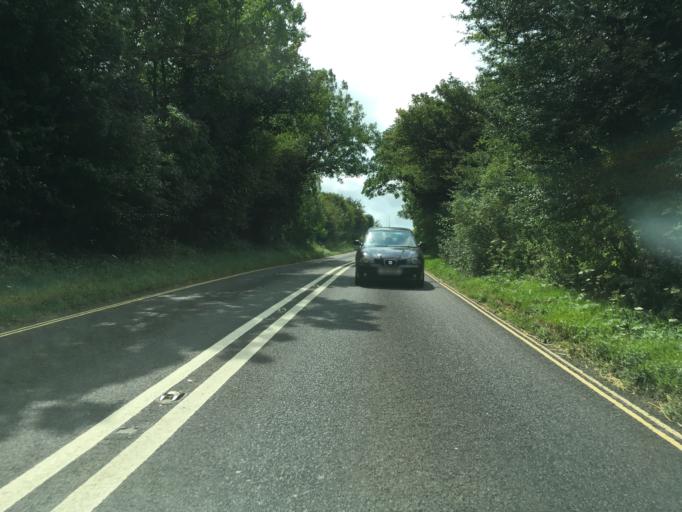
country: GB
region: England
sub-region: Brighton and Hove
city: Rottingdean
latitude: 50.8582
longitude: -0.0774
